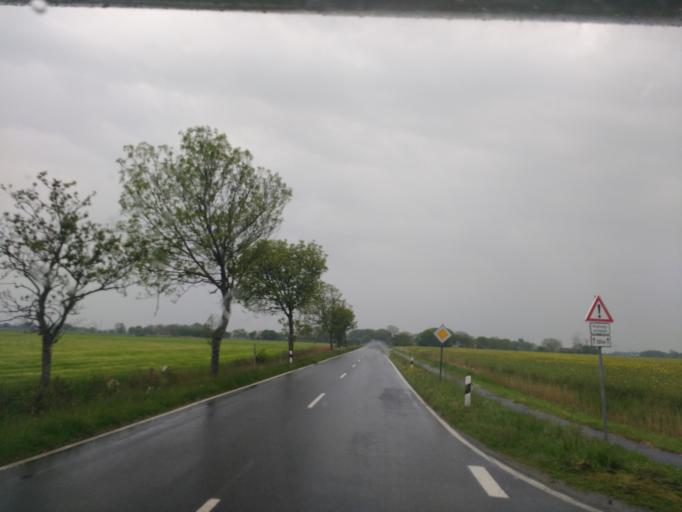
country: DE
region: Lower Saxony
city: Wangerooge
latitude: 53.6926
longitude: 7.9041
